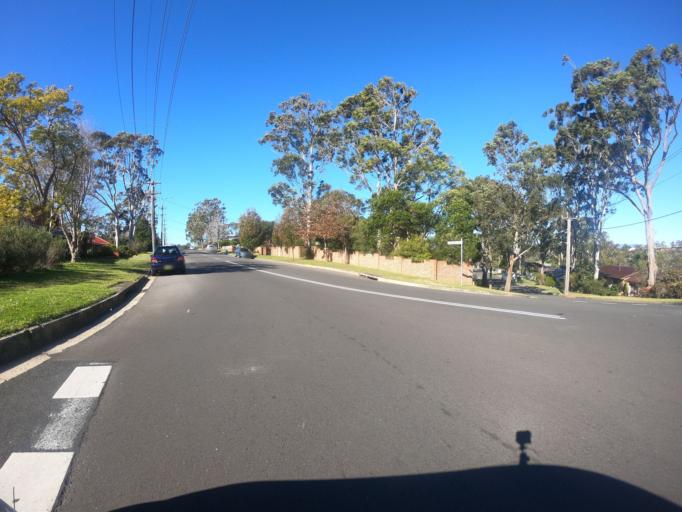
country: AU
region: New South Wales
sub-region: Wollongong
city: Mount Keira
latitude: -34.4251
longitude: 150.8509
